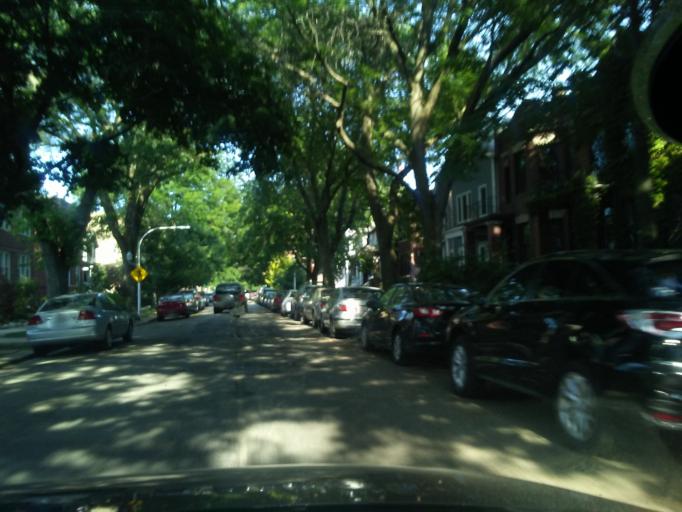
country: US
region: Illinois
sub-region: Cook County
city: Lincolnwood
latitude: 41.9752
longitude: -87.6712
